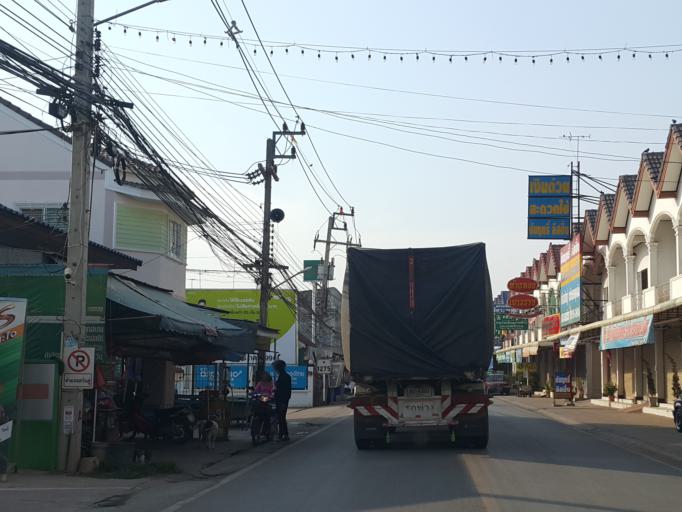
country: TH
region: Phitsanulok
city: Phrom Phiram
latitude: 17.0332
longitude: 100.1998
